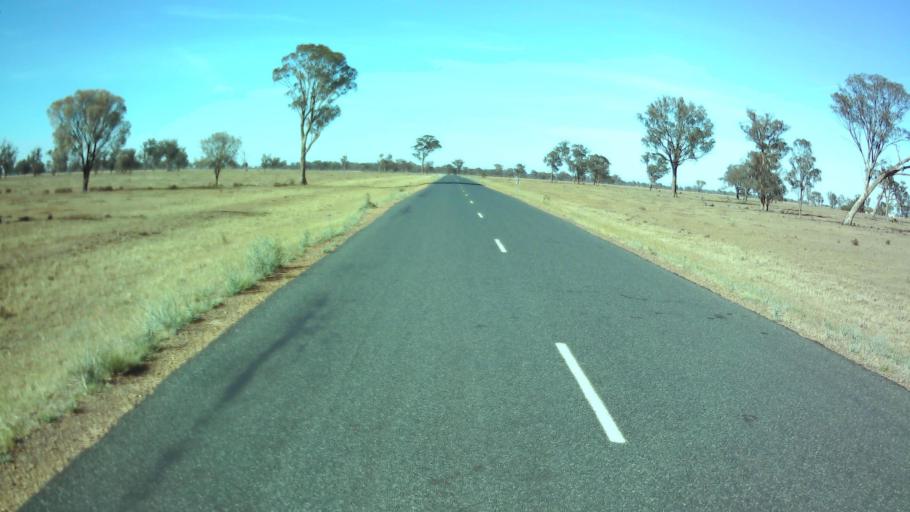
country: AU
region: New South Wales
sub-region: Weddin
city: Grenfell
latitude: -34.0462
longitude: 147.9241
